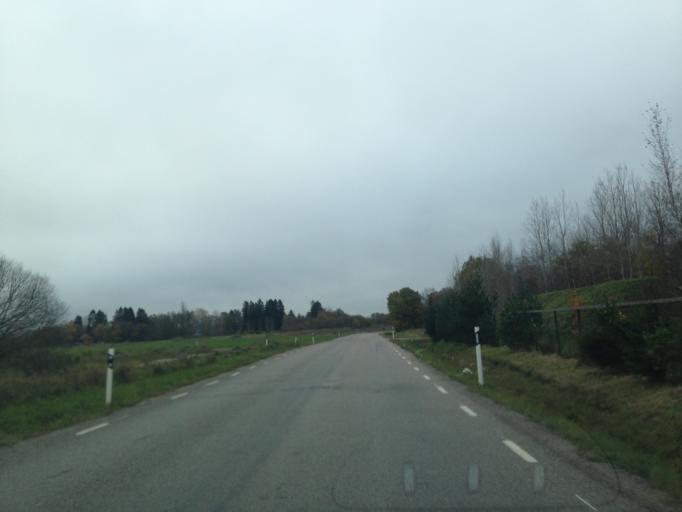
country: EE
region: Harju
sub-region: Saue linn
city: Saue
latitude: 59.3646
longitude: 24.5474
